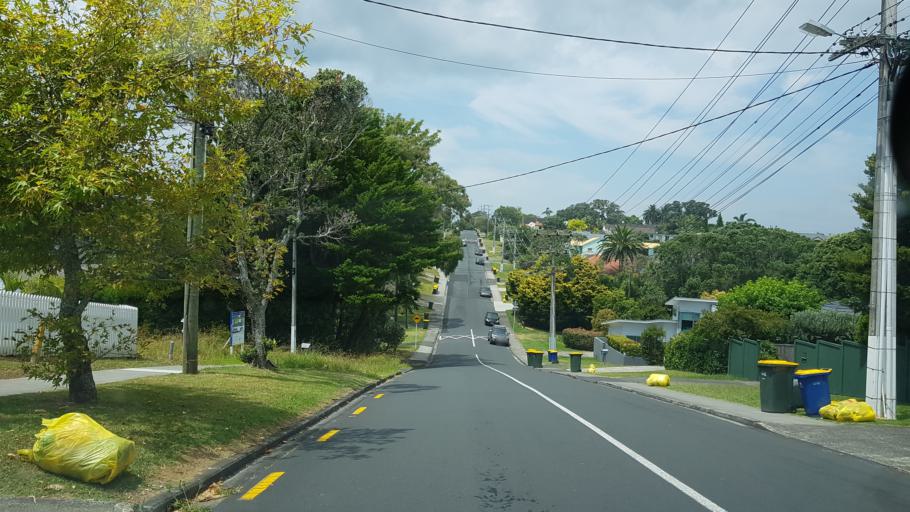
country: NZ
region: Auckland
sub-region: Auckland
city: North Shore
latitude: -36.8013
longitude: 174.7811
